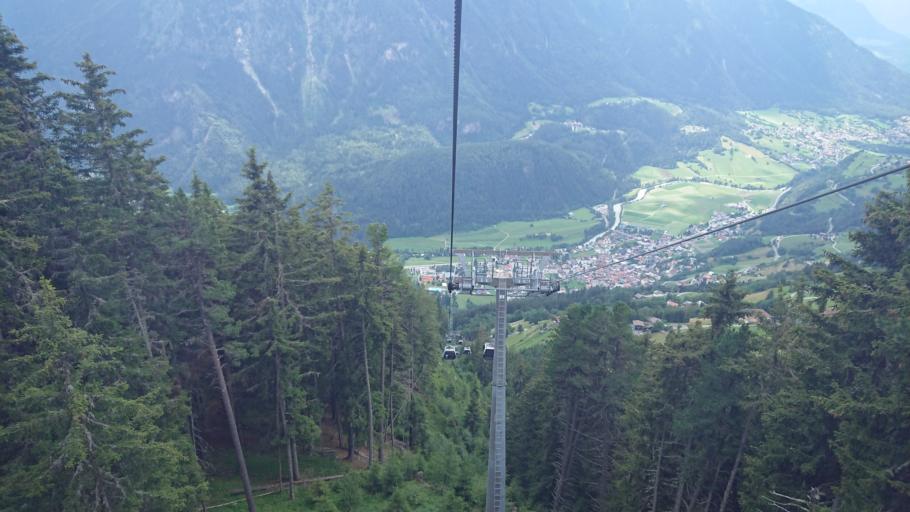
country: AT
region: Tyrol
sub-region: Politischer Bezirk Imst
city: Oetz
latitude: 47.2086
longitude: 10.9237
